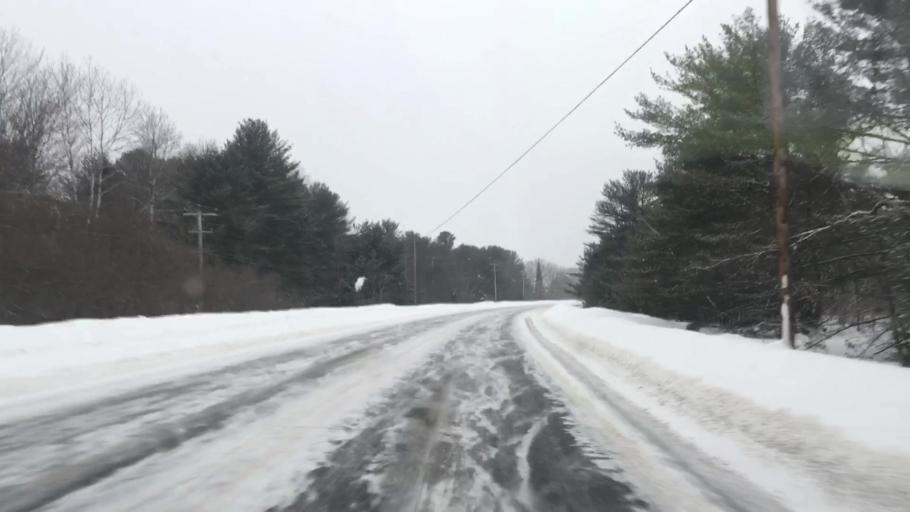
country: US
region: Maine
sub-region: Penobscot County
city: Medway
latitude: 45.5645
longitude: -68.3986
